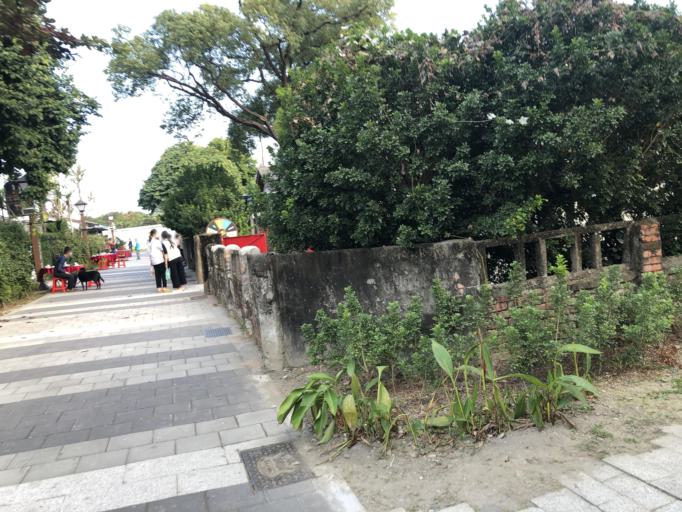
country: TW
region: Taiwan
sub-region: Pingtung
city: Pingtung
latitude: 22.6780
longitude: 120.4835
